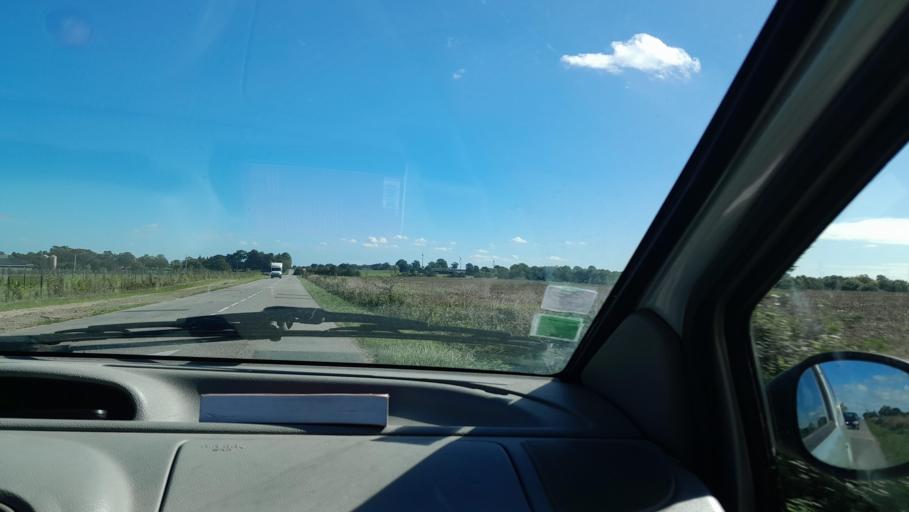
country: FR
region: Pays de la Loire
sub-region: Departement de la Mayenne
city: Cosse-le-Vivien
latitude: 47.9386
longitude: -0.8706
